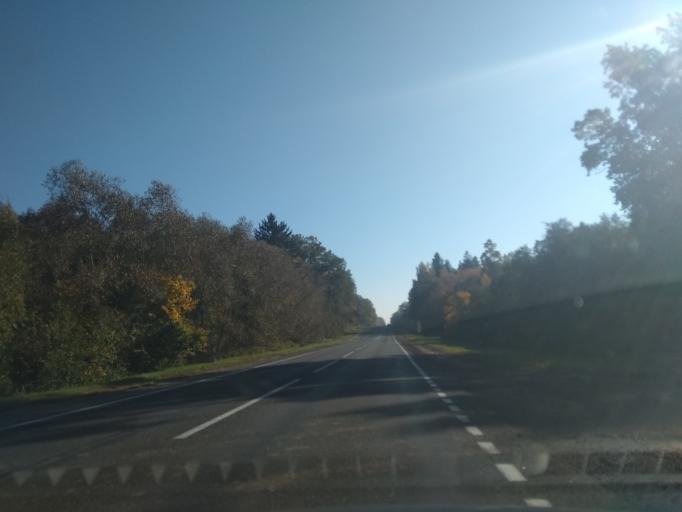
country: BY
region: Grodnenskaya
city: Slonim
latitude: 53.1115
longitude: 25.1647
